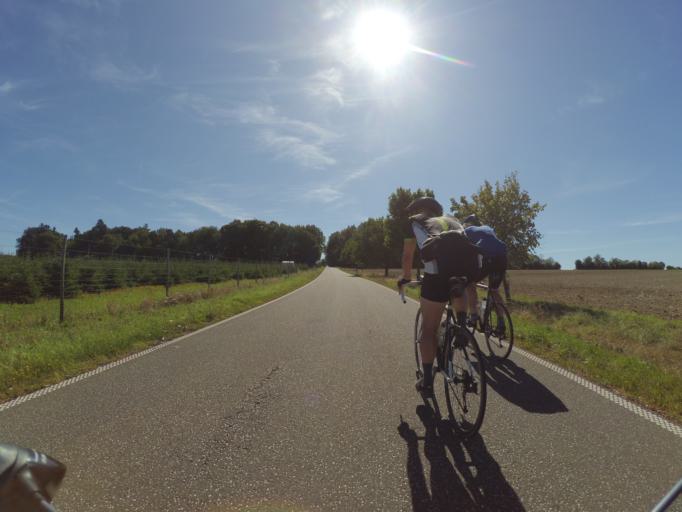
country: DE
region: Rheinland-Pfalz
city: Morbach
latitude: 49.8016
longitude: 7.0797
